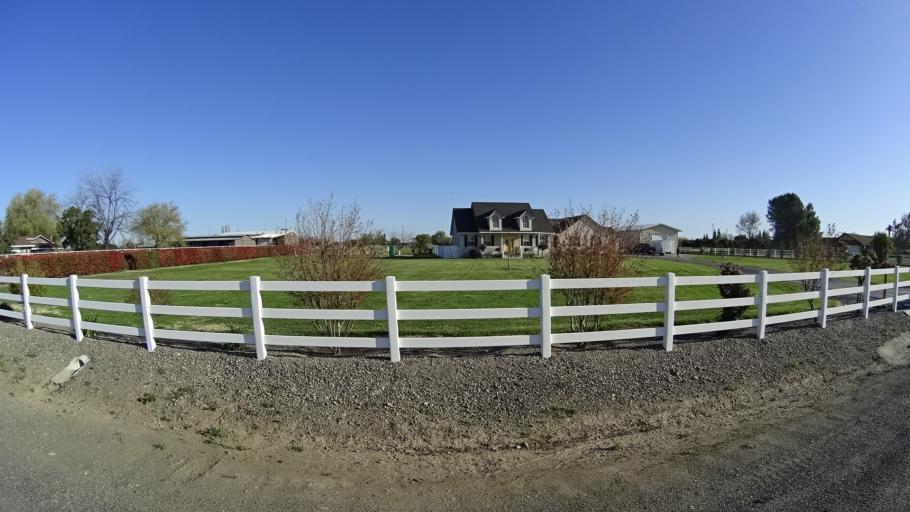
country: US
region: California
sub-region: Glenn County
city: Orland
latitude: 39.7590
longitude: -122.2329
